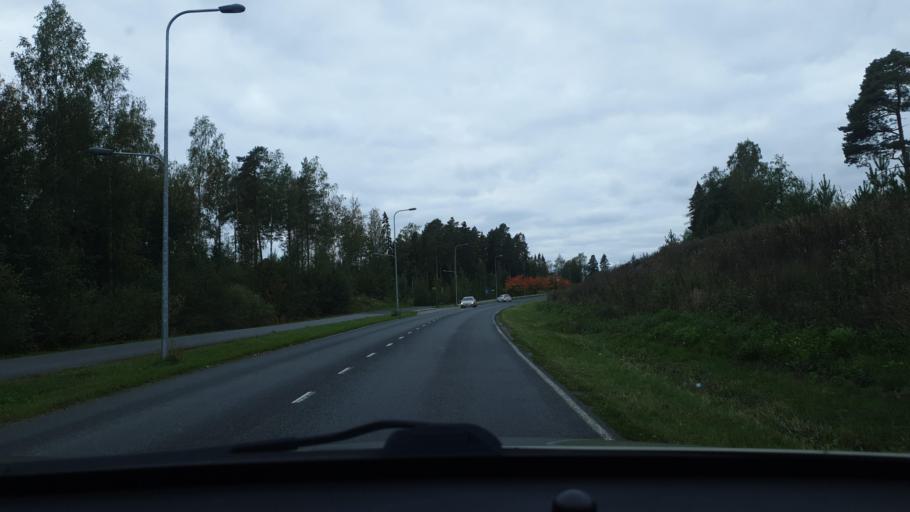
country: FI
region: Ostrobothnia
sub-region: Vaasa
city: Korsholm
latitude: 63.1021
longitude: 21.6833
